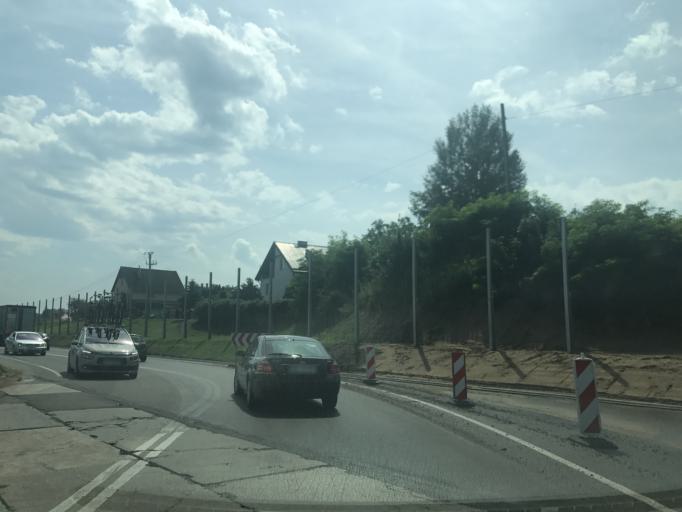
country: PL
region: Warmian-Masurian Voivodeship
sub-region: Powiat ostrodzki
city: Ostroda
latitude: 53.6974
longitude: 19.9826
